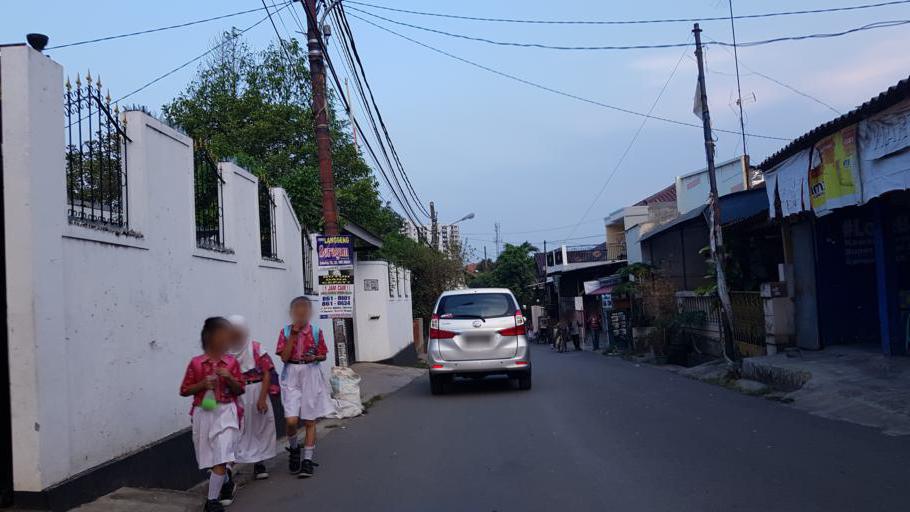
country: ID
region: West Java
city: Bekasi
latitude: -6.2657
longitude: 106.9467
